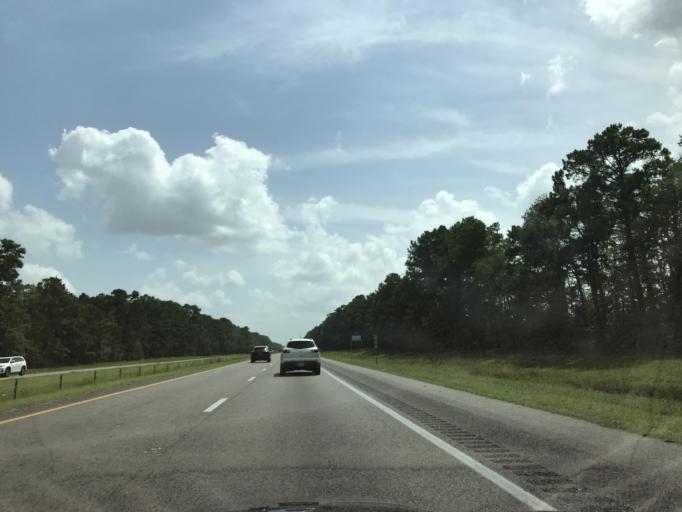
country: US
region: North Carolina
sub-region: Pender County
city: Rocky Point
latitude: 34.4997
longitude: -77.8770
